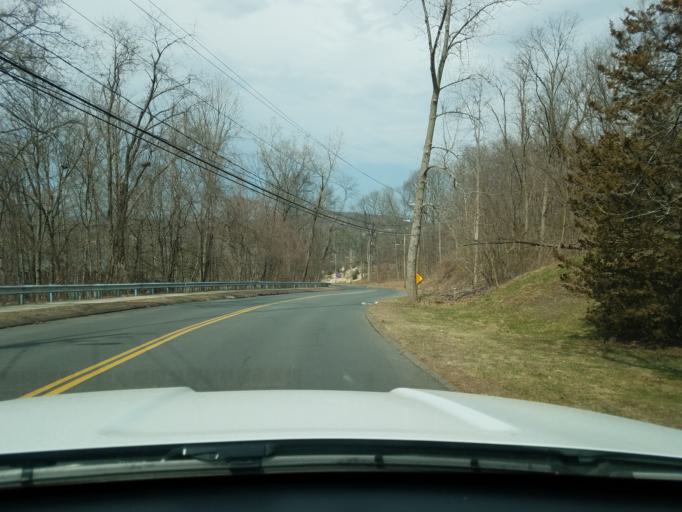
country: US
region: Connecticut
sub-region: Hartford County
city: Newington
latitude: 41.6768
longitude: -72.7095
